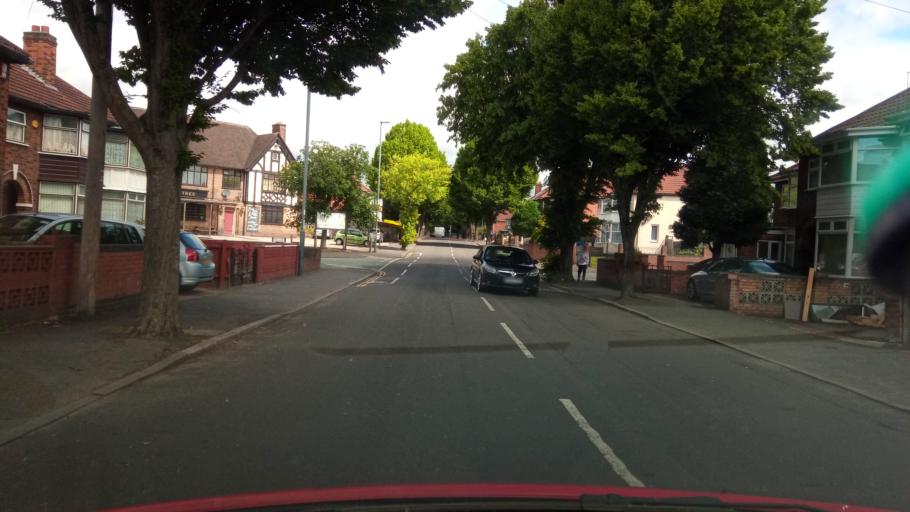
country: GB
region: England
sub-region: Derby
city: Derby
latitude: 52.8995
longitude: -1.4746
